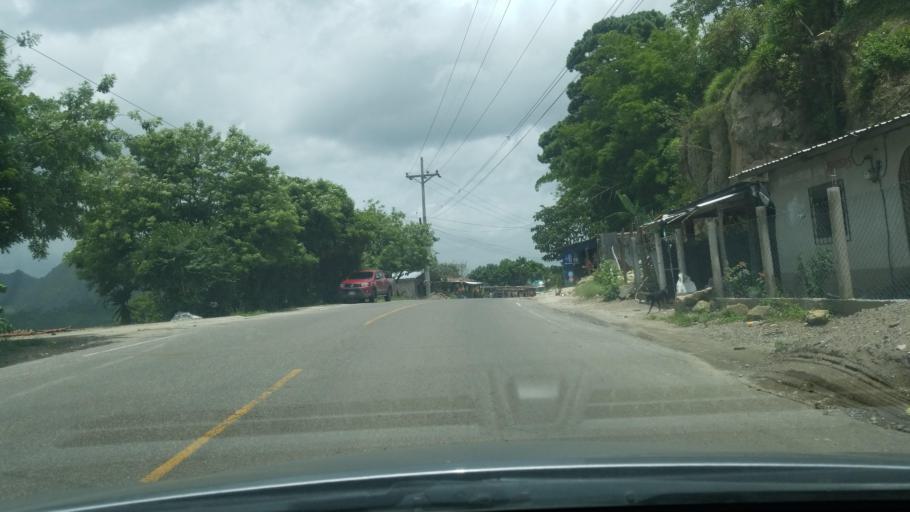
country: HN
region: Copan
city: Ojos de Agua
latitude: 14.6815
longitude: -88.8183
